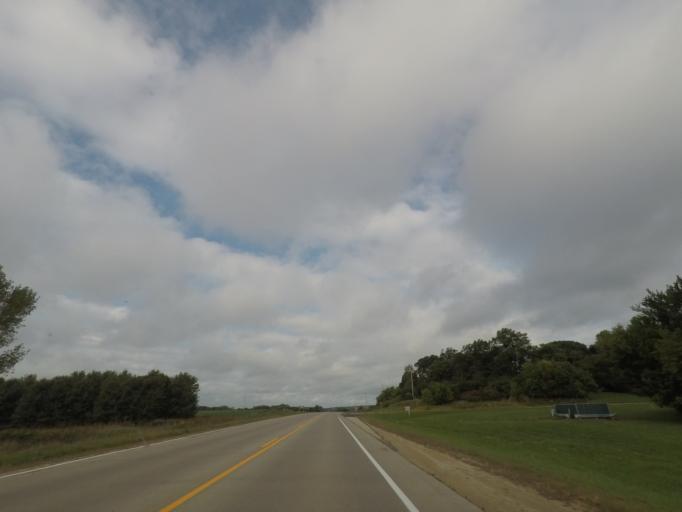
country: US
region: Wisconsin
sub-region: Dane County
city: Deerfield
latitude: 43.0202
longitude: -89.0539
